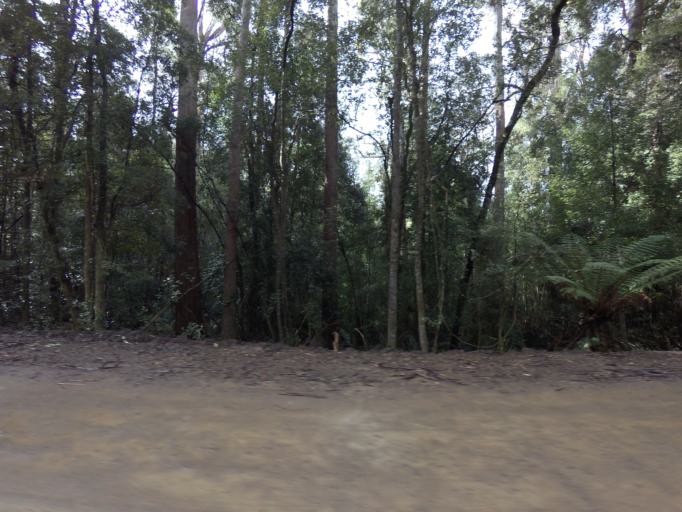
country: AU
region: Tasmania
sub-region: Huon Valley
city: Geeveston
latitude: -43.5736
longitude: 146.8883
